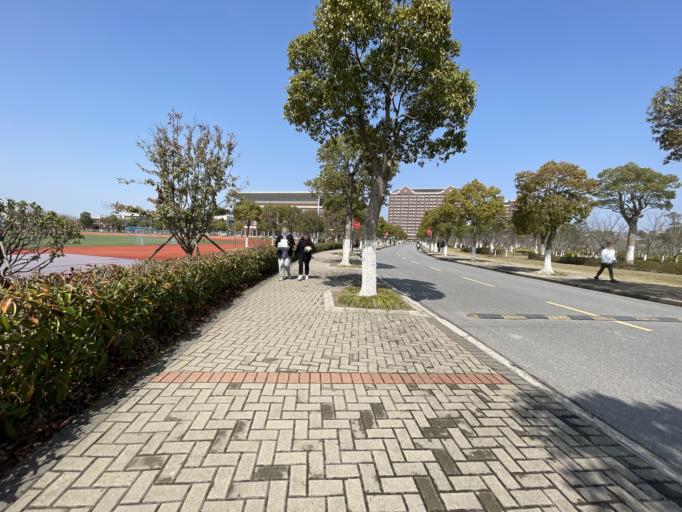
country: CN
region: Shanghai Shi
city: Shuyuan
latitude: 30.8933
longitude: 121.8850
